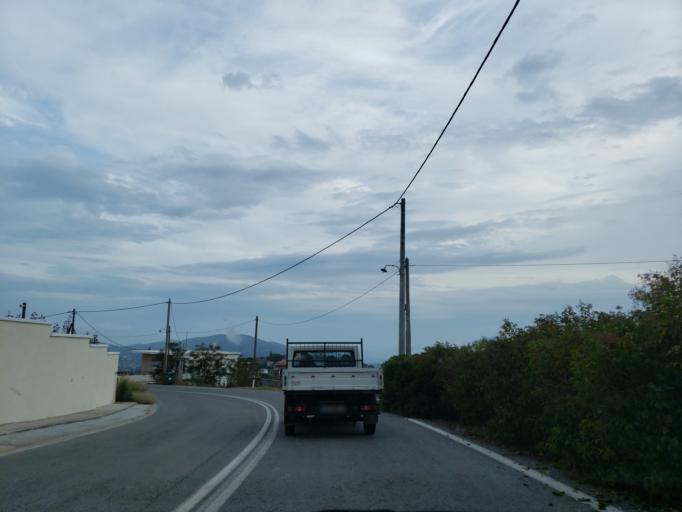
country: GR
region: Attica
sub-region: Nomarchia Anatolikis Attikis
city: Grammatiko
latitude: 38.2045
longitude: 23.9604
